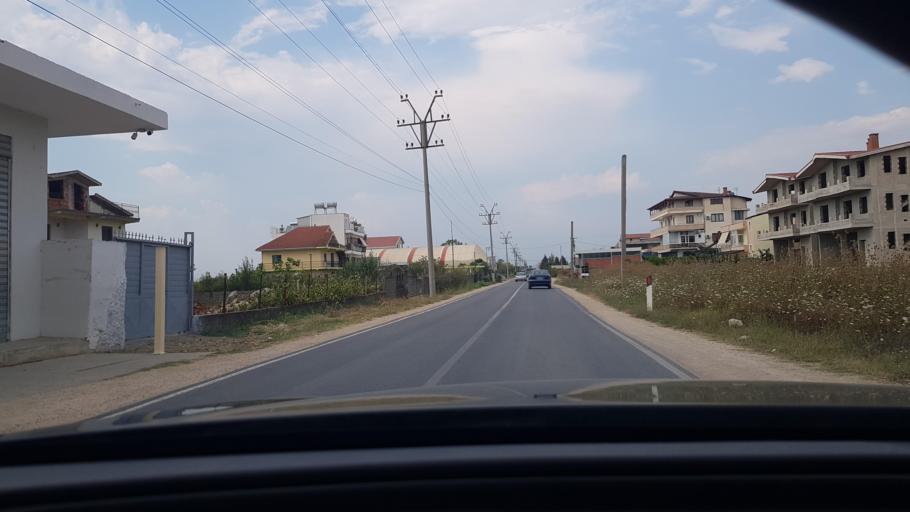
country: AL
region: Durres
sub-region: Rrethi i Durresit
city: Sukth
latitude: 41.4048
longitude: 19.5467
